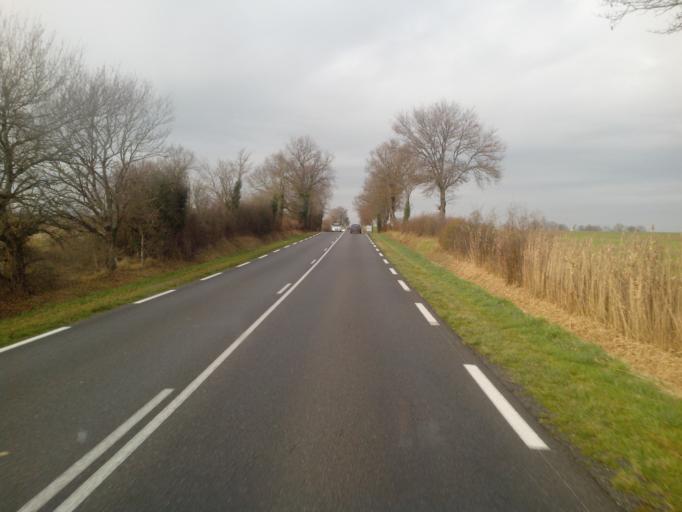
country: FR
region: Limousin
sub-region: Departement de la Haute-Vienne
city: Bussiere-Poitevine
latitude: 46.2934
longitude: 0.8439
